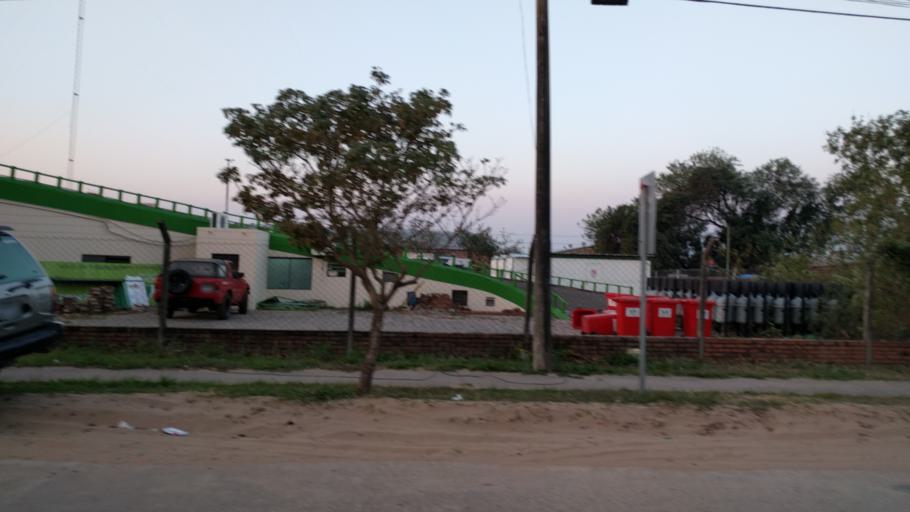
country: BO
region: Santa Cruz
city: Santa Cruz de la Sierra
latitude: -17.7596
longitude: -63.1472
